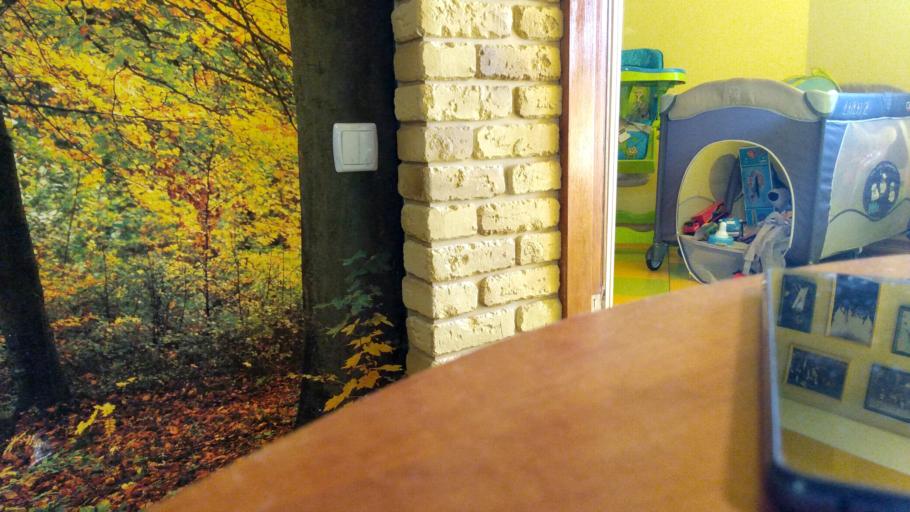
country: RU
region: Tverskaya
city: Kalashnikovo
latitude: 57.3601
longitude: 35.2297
